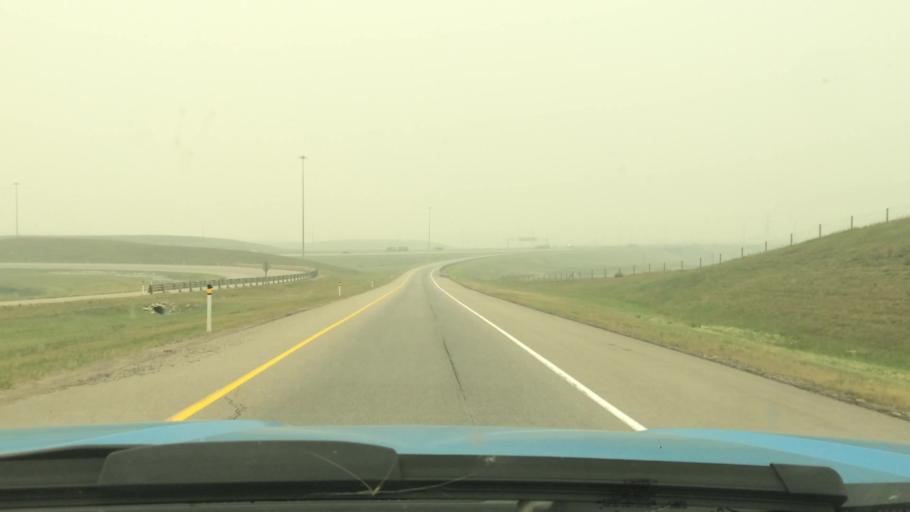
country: CA
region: Alberta
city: Airdrie
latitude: 51.1787
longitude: -114.0048
